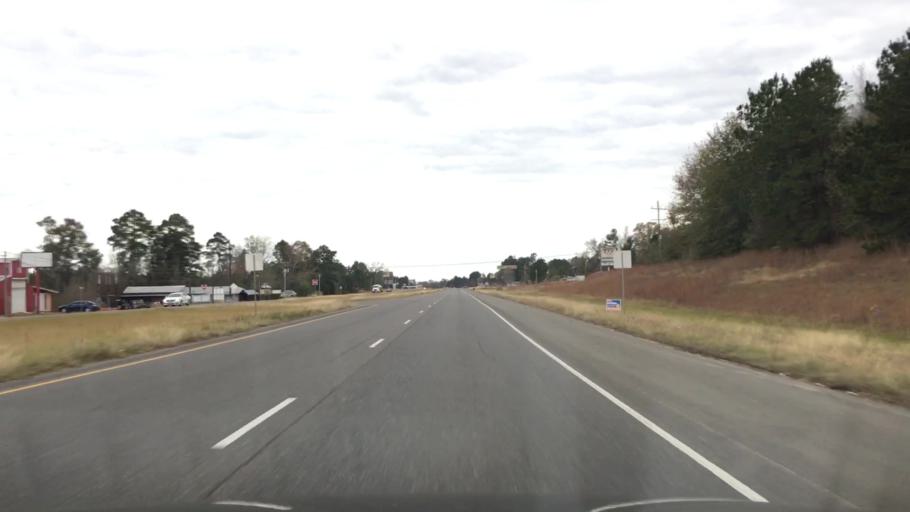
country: US
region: Louisiana
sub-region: Vernon Parish
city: New Llano
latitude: 31.0832
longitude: -93.2721
